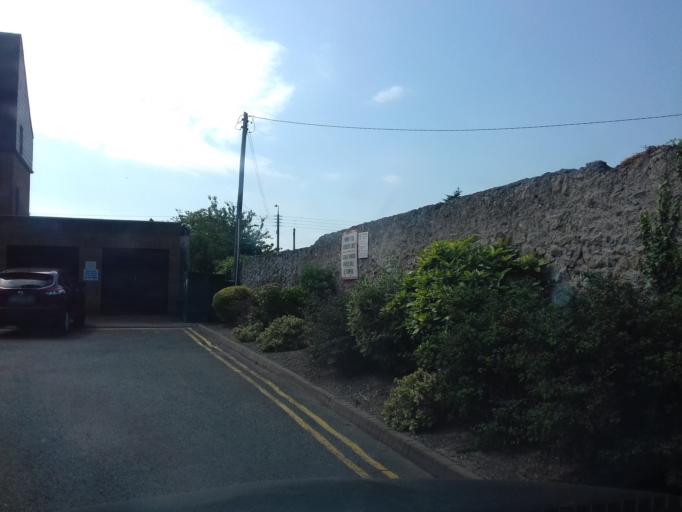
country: IE
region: Leinster
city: Sutton
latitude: 53.3894
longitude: -6.1205
